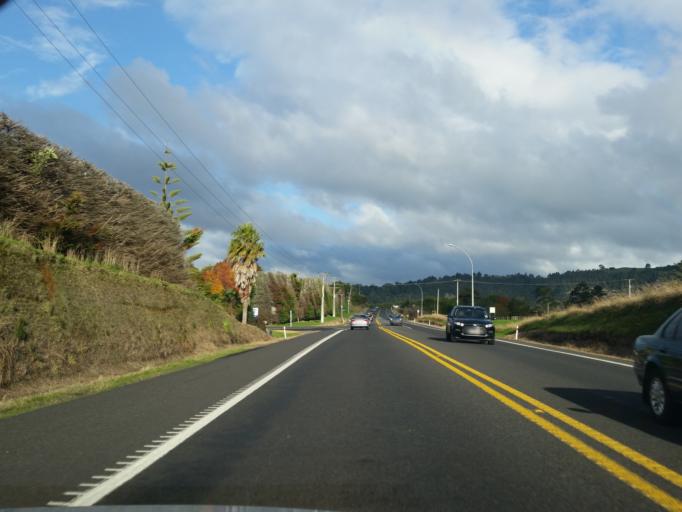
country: NZ
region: Bay of Plenty
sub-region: Tauranga City
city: Tauranga
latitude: -37.6861
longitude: 176.0380
